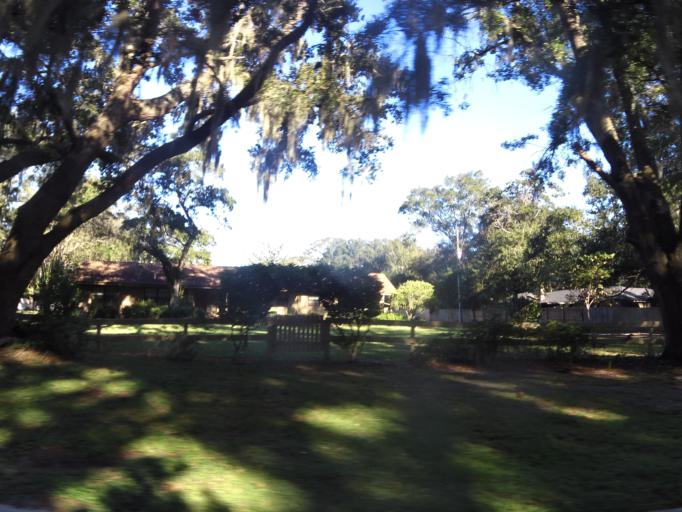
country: US
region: Florida
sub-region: Duval County
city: Atlantic Beach
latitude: 30.3305
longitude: -81.4518
